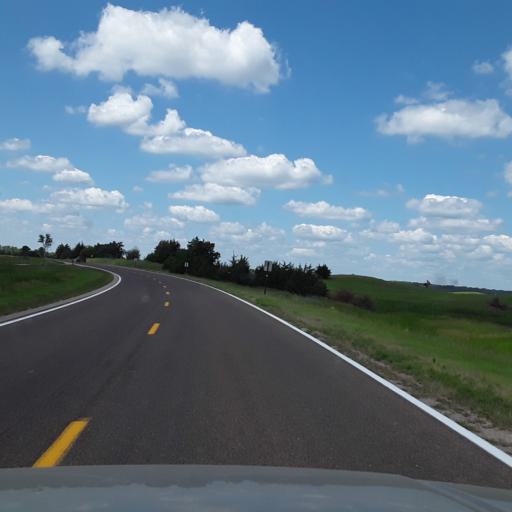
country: US
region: Nebraska
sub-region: Nance County
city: Genoa
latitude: 41.3979
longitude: -97.6953
